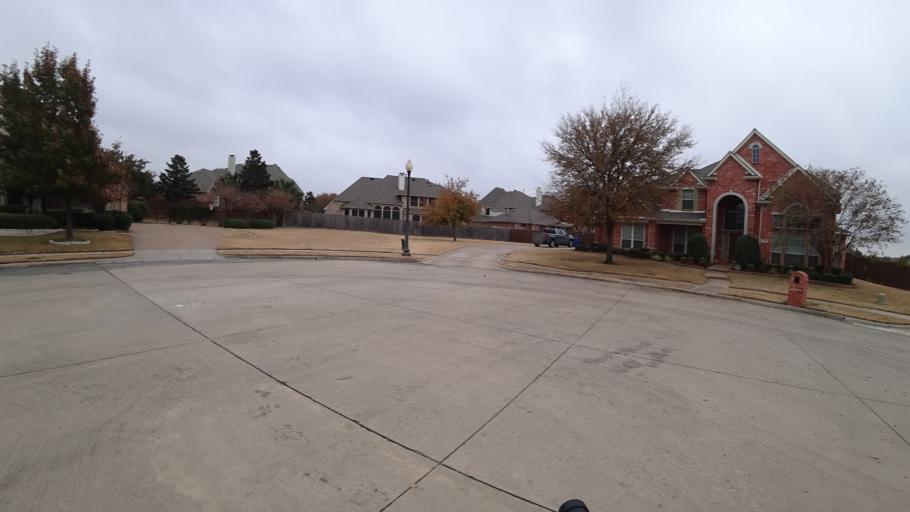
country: US
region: Texas
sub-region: Denton County
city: Lewisville
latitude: 33.0336
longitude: -96.9329
